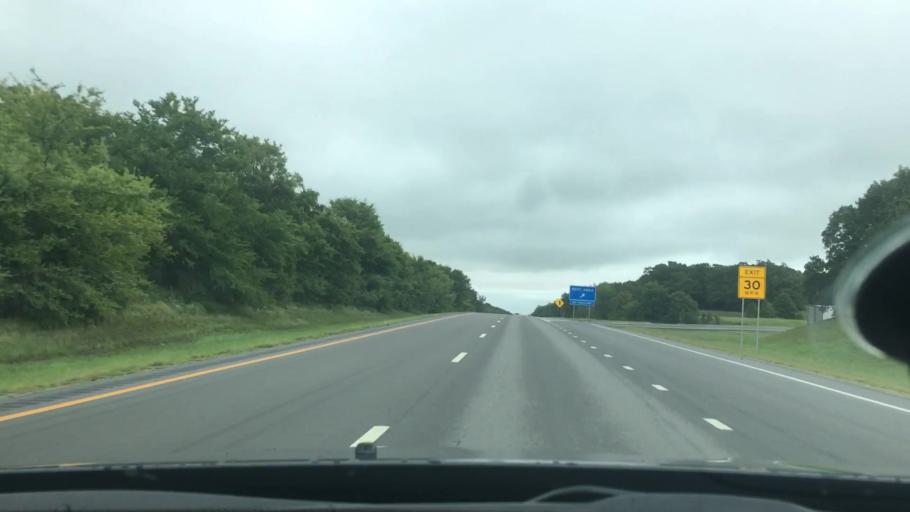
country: US
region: Oklahoma
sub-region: Okmulgee County
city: Morris
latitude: 35.4361
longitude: -95.7912
